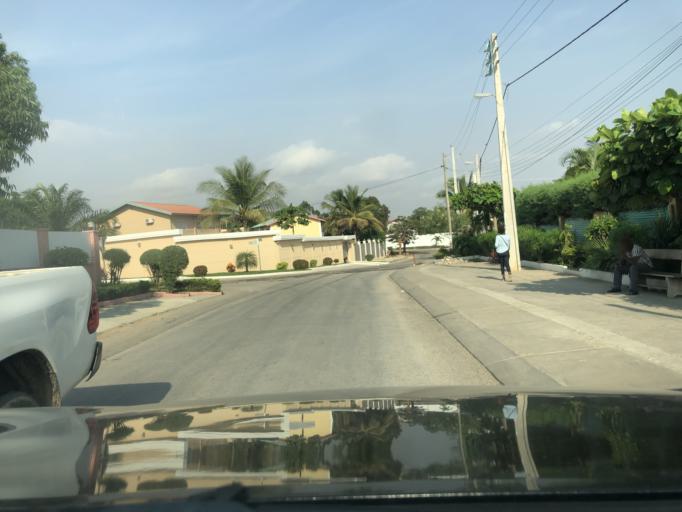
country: AO
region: Luanda
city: Luanda
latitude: -8.9091
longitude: 13.2271
